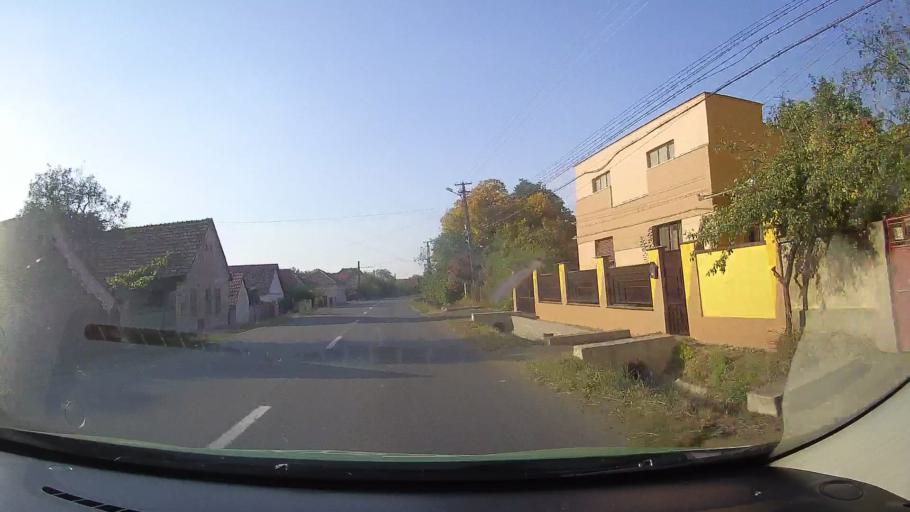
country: RO
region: Arad
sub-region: Comuna Ghioroc
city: Ghioroc
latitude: 46.1457
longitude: 21.5980
